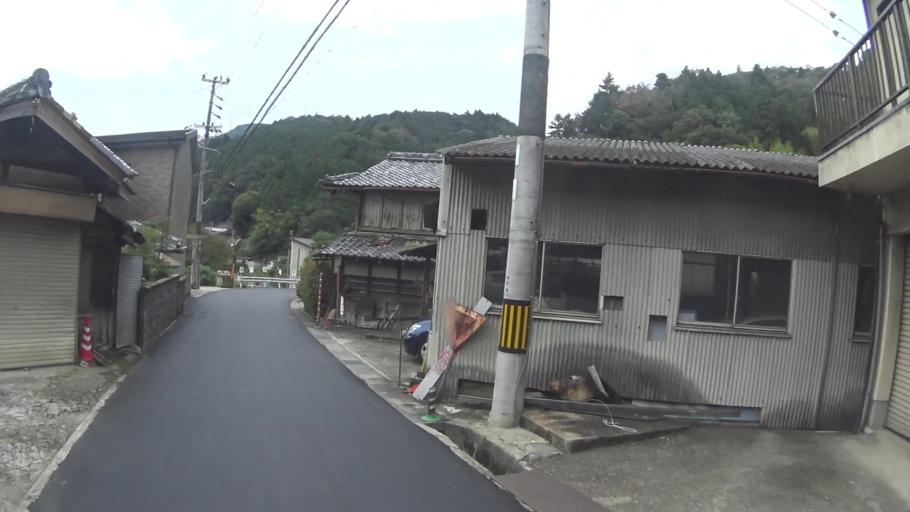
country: JP
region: Kyoto
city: Uji
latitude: 34.8306
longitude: 135.9487
